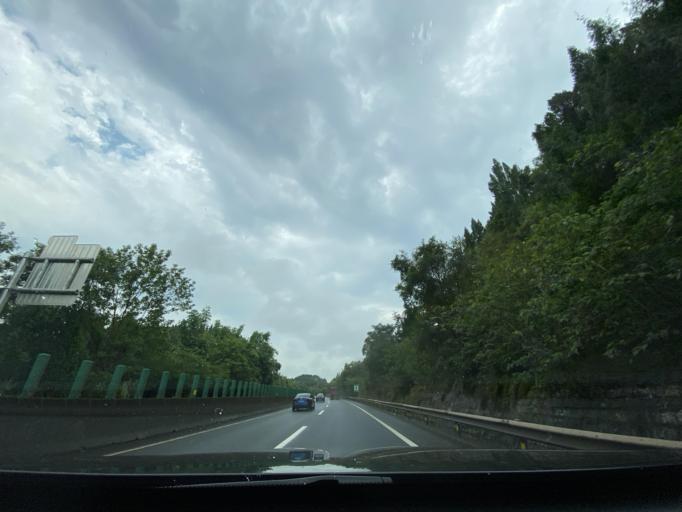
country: CN
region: Sichuan
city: Yanjiang
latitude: 30.1207
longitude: 104.5974
